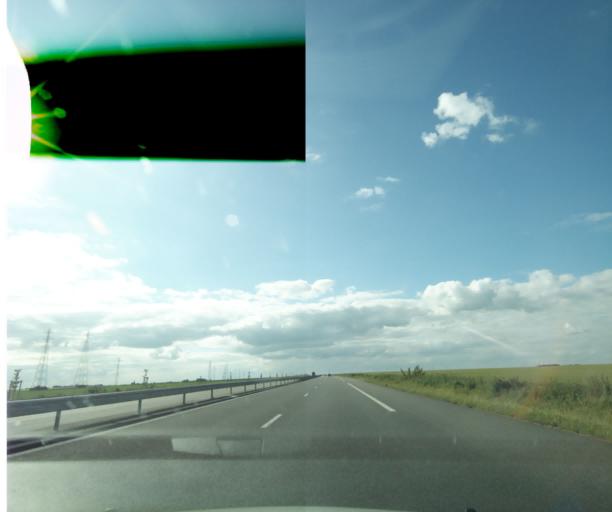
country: FR
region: Centre
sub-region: Departement d'Eure-et-Loir
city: Sours
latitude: 48.3486
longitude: 1.6250
